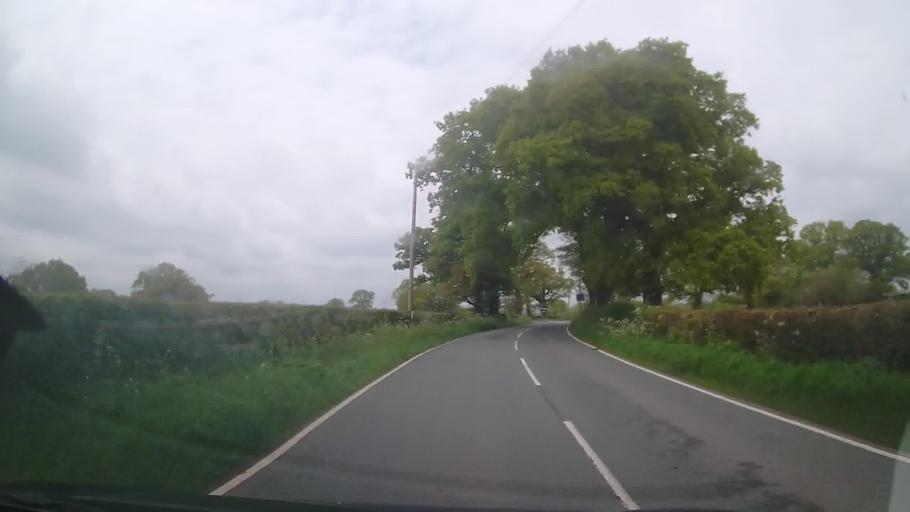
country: GB
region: England
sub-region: Shropshire
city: Ellesmere
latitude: 52.9521
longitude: -2.8379
